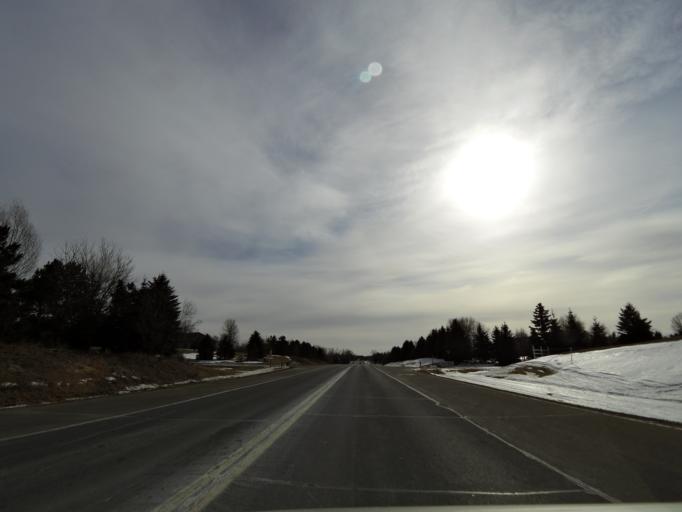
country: US
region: Minnesota
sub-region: Washington County
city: Lake Elmo
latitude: 44.9800
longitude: -92.8600
